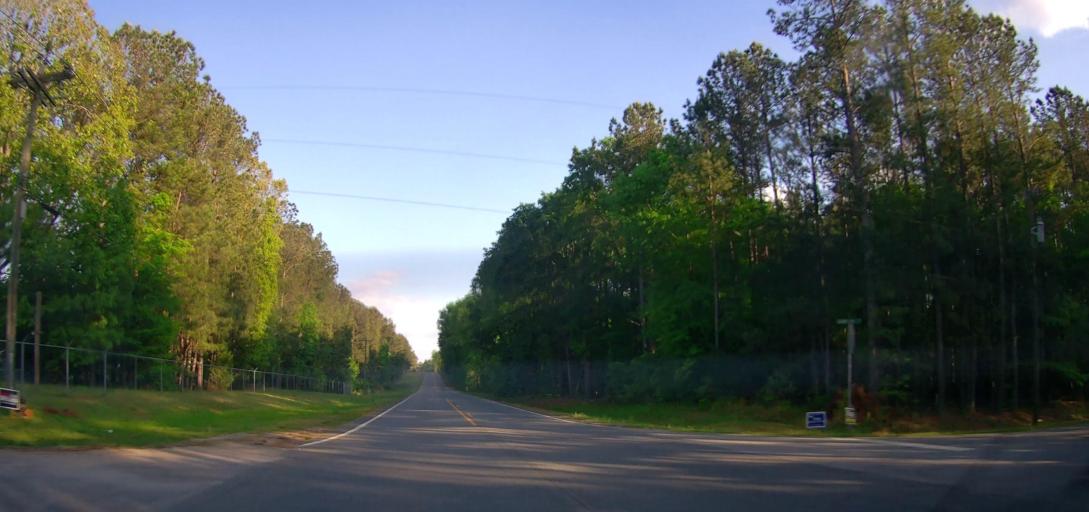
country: US
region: Georgia
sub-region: Putnam County
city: Eatonton
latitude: 33.3186
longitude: -83.4964
